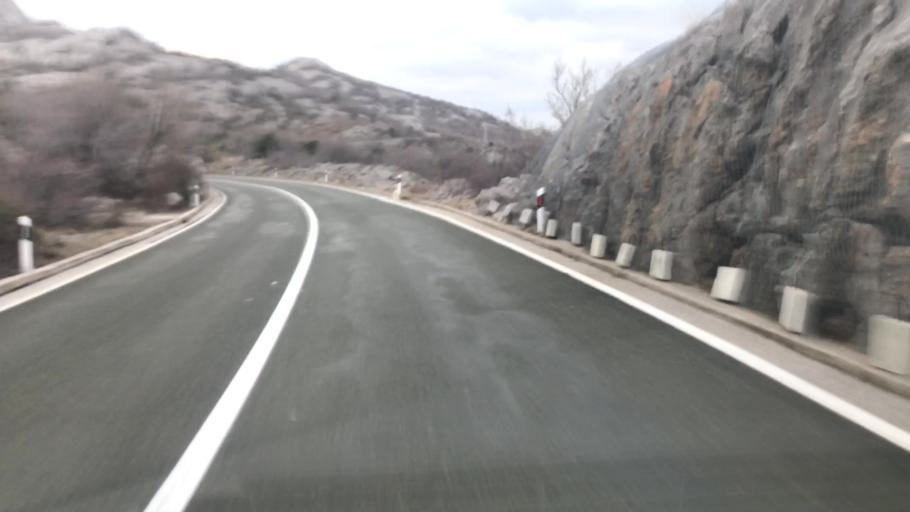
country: HR
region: Licko-Senjska
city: Novalja
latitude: 44.6678
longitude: 14.9437
